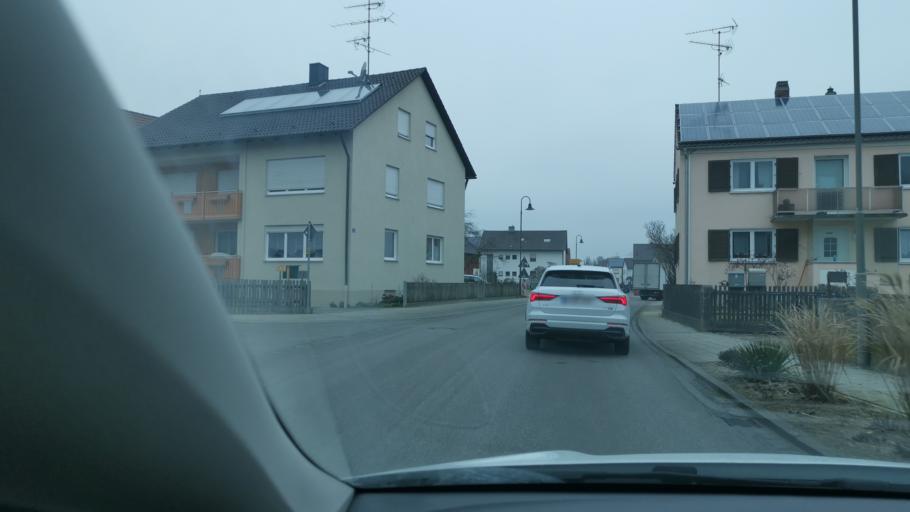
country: DE
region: Bavaria
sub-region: Swabia
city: Thierhaupten
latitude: 48.5658
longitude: 10.9086
